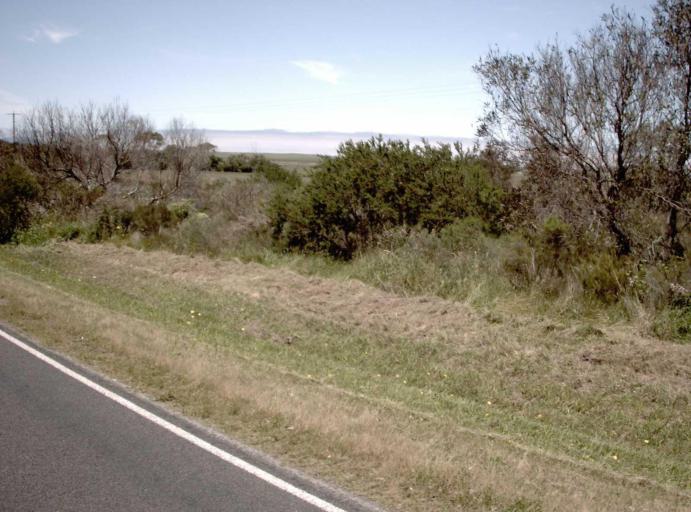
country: AU
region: Victoria
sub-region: Latrobe
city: Morwell
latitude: -38.7901
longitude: 146.1763
